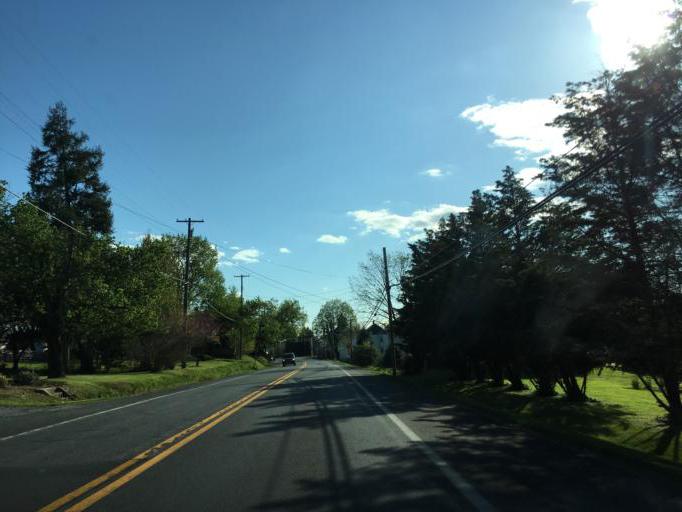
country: US
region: Maryland
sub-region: Frederick County
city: Woodsboro
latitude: 39.5658
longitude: -77.2934
